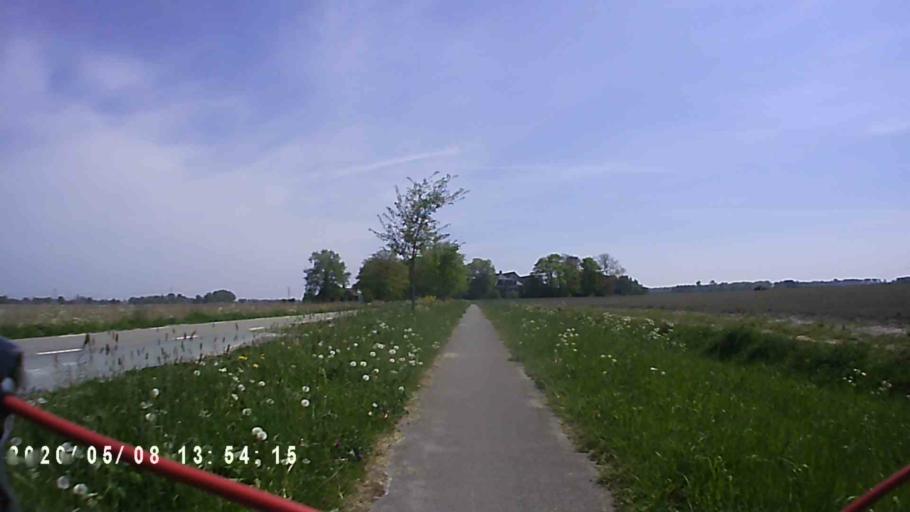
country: NL
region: Groningen
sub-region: Gemeente Appingedam
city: Appingedam
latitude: 53.3372
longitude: 6.7867
